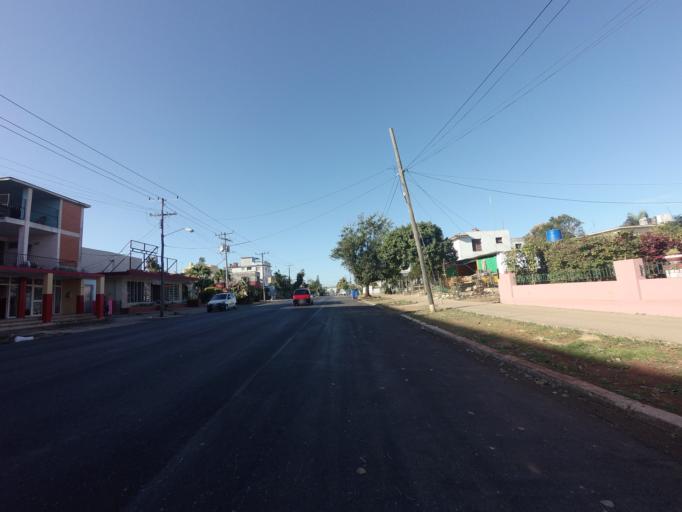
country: CU
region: La Habana
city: Cerro
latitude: 23.1025
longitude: -82.4344
